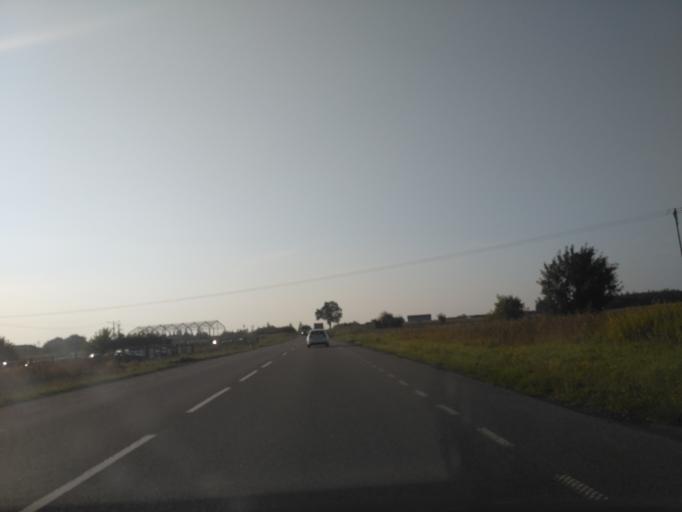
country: PL
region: Lublin Voivodeship
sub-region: Powiat janowski
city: Modliborzyce
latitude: 50.7438
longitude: 22.3435
